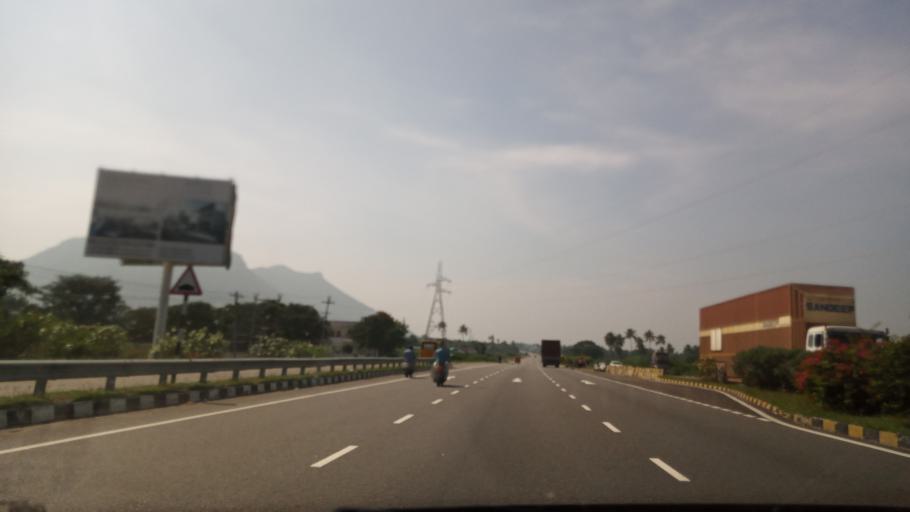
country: IN
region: Tamil Nadu
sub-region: Vellore
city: Pallikondai
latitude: 12.9104
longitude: 78.9901
